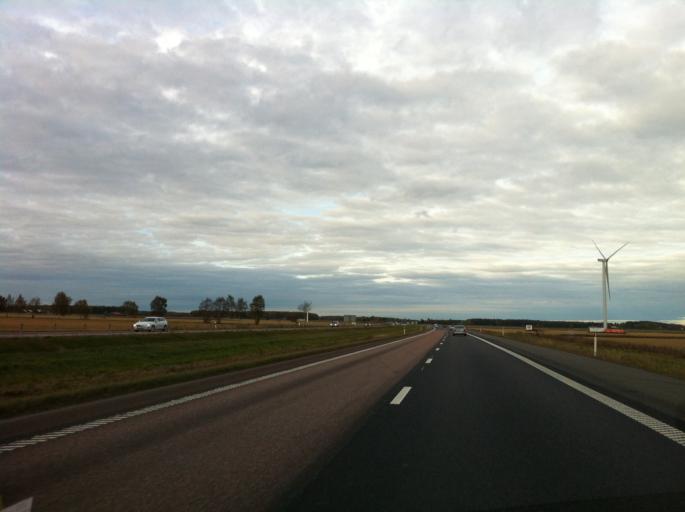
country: SE
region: OErebro
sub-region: Kumla Kommun
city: Kumla
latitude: 59.1616
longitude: 15.1075
